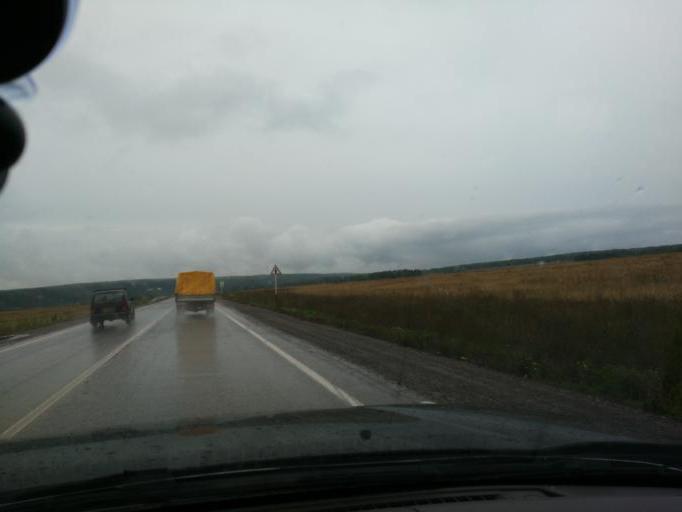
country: RU
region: Perm
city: Yugo-Kamskiy
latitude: 57.7049
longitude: 55.6282
